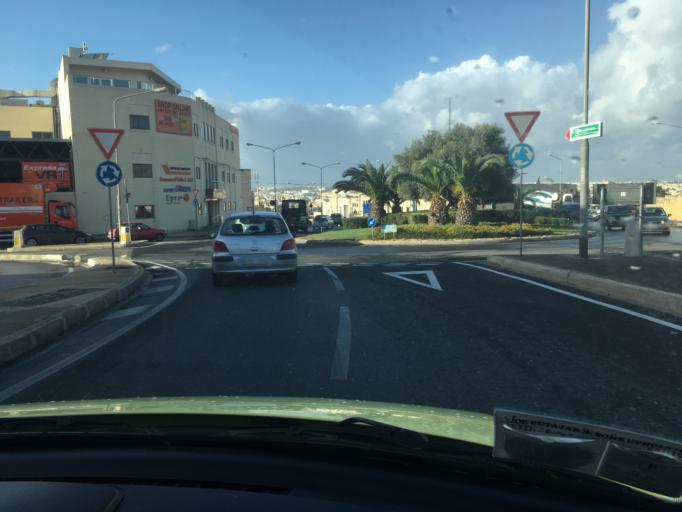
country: MT
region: Qormi
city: Qormi
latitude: 35.8678
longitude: 14.4806
